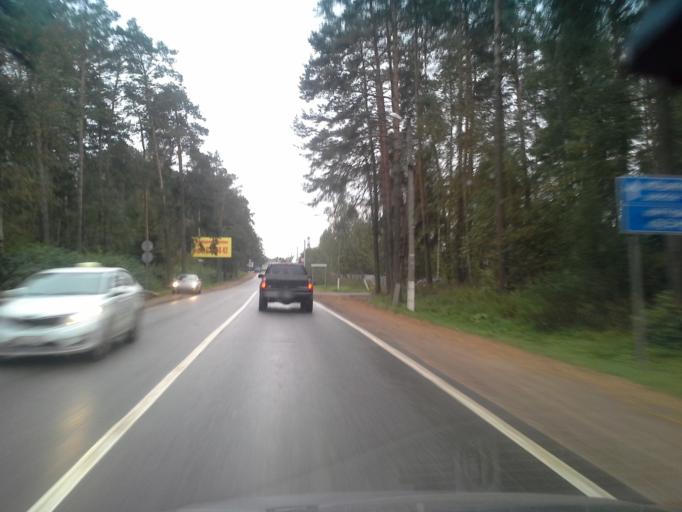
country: RU
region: Moskovskaya
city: Petrovo-Dal'neye
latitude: 55.7635
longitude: 37.1680
